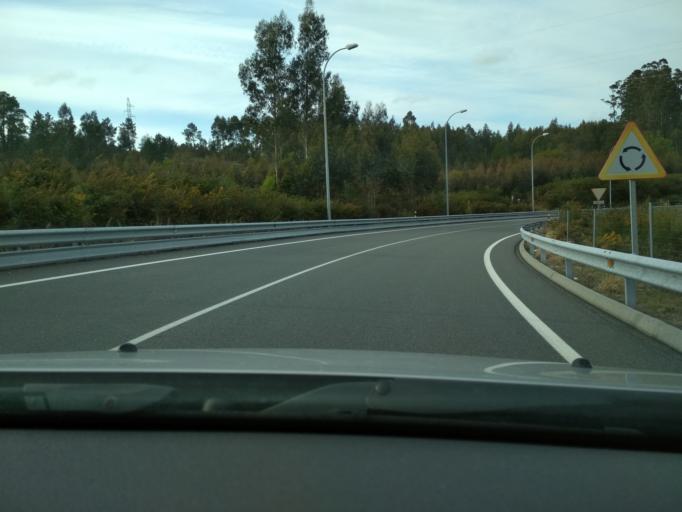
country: ES
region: Galicia
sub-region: Provincia da Coruna
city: Culleredo
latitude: 43.2927
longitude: -8.4041
